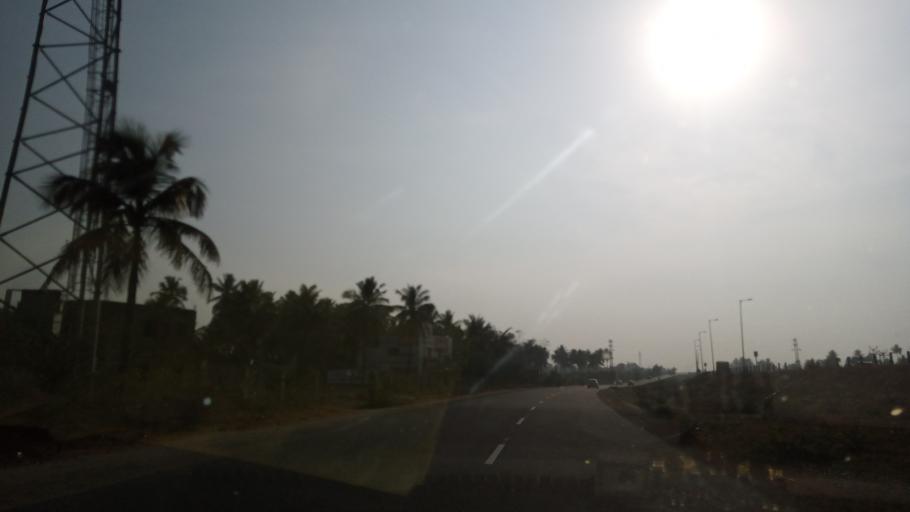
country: IN
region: Tamil Nadu
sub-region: Salem
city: Salem
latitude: 11.6643
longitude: 78.2337
